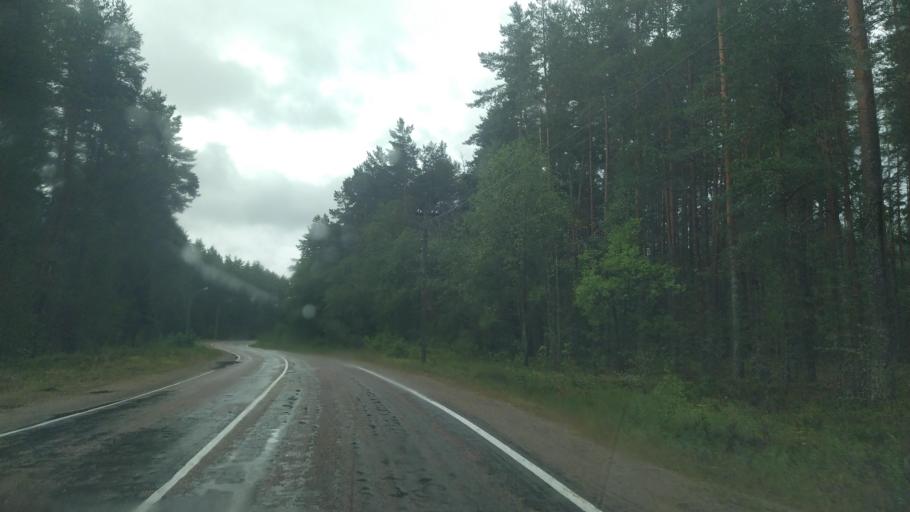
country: RU
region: Leningrad
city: Priozersk
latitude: 60.9687
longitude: 30.2852
